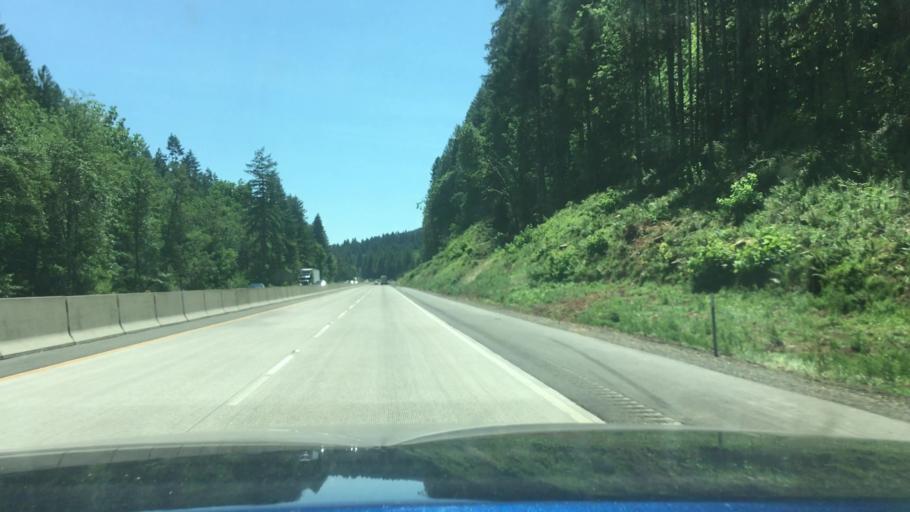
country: US
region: Oregon
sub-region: Douglas County
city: Yoncalla
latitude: 43.6784
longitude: -123.1984
